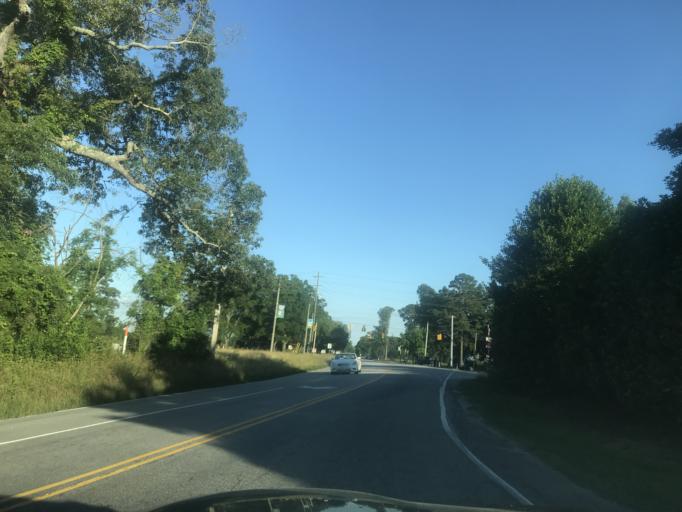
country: US
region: North Carolina
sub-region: Johnston County
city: Archer Lodge
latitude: 35.6930
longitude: -78.3736
